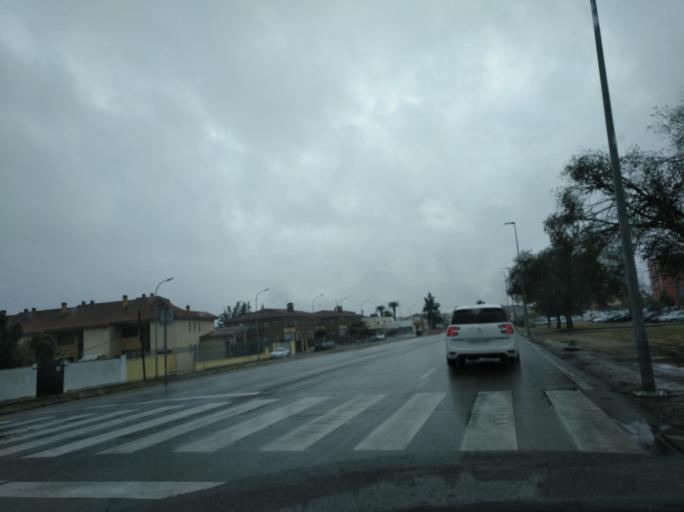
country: ES
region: Extremadura
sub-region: Provincia de Badajoz
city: Badajoz
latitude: 38.8864
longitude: -6.9894
